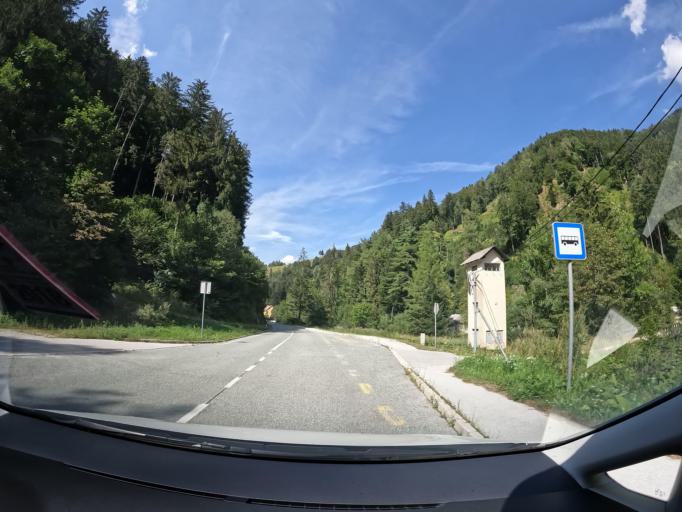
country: SI
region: Preddvor
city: Preddvor
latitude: 46.3742
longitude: 14.4025
